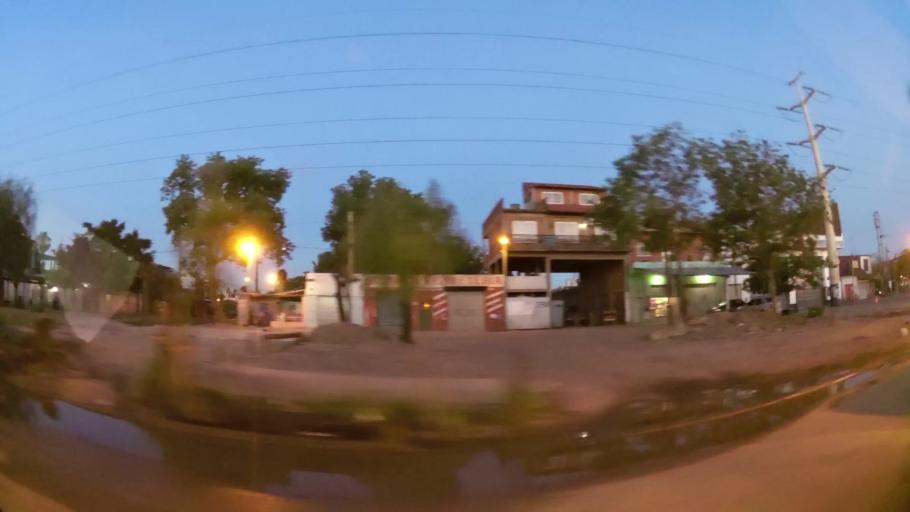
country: AR
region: Buenos Aires
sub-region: Partido de Almirante Brown
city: Adrogue
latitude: -34.7721
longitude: -58.3238
